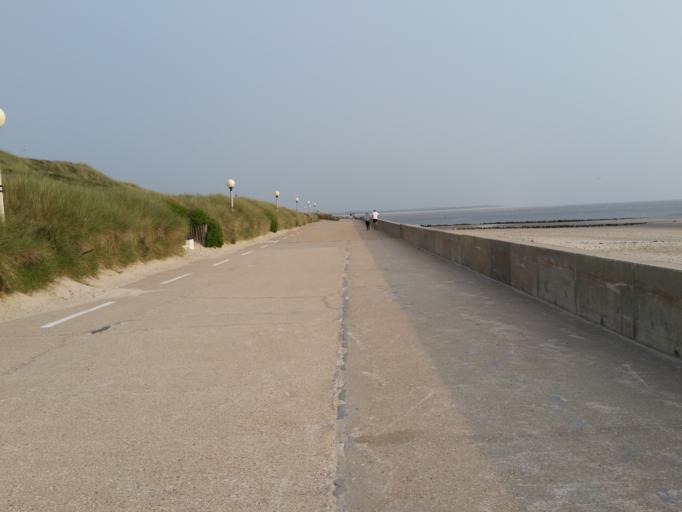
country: FR
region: Nord-Pas-de-Calais
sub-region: Departement du Pas-de-Calais
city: Berck-Plage
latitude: 50.3990
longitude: 1.5558
